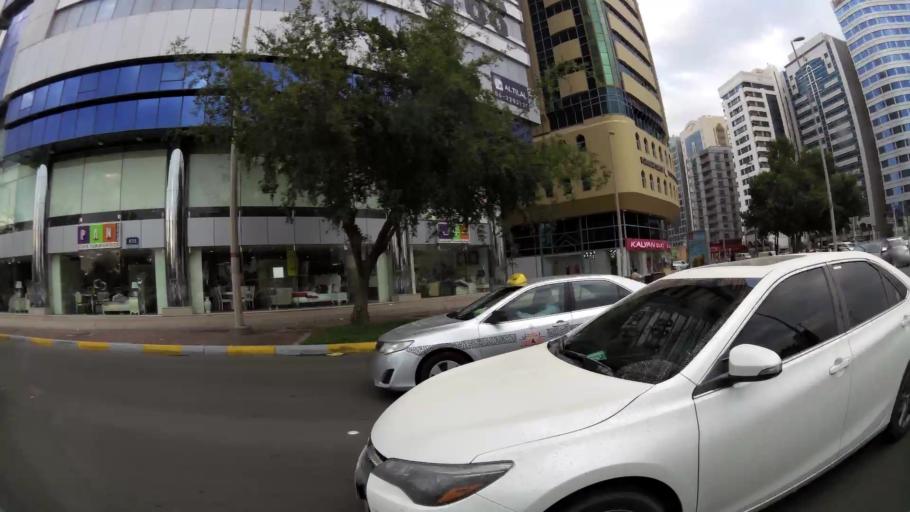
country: AE
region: Abu Dhabi
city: Abu Dhabi
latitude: 24.4763
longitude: 54.3652
